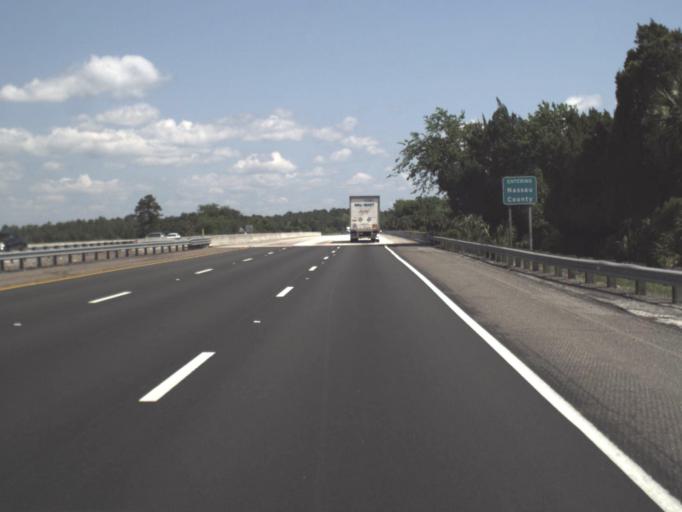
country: US
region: Florida
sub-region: Nassau County
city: Yulee
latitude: 30.5743
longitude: -81.6454
